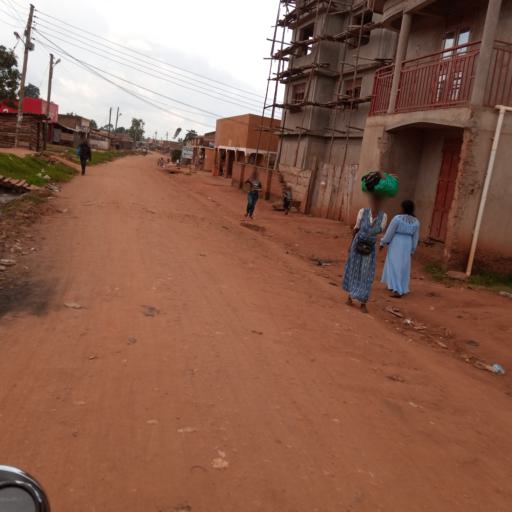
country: UG
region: Eastern Region
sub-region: Mbale District
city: Mbale
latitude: 1.0934
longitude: 34.1742
